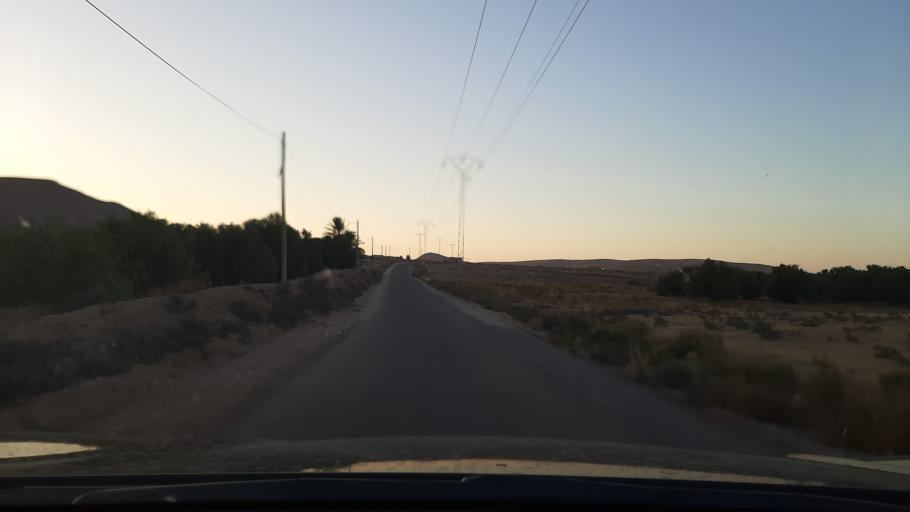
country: TN
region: Qabis
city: Matmata
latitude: 33.5478
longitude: 10.1906
